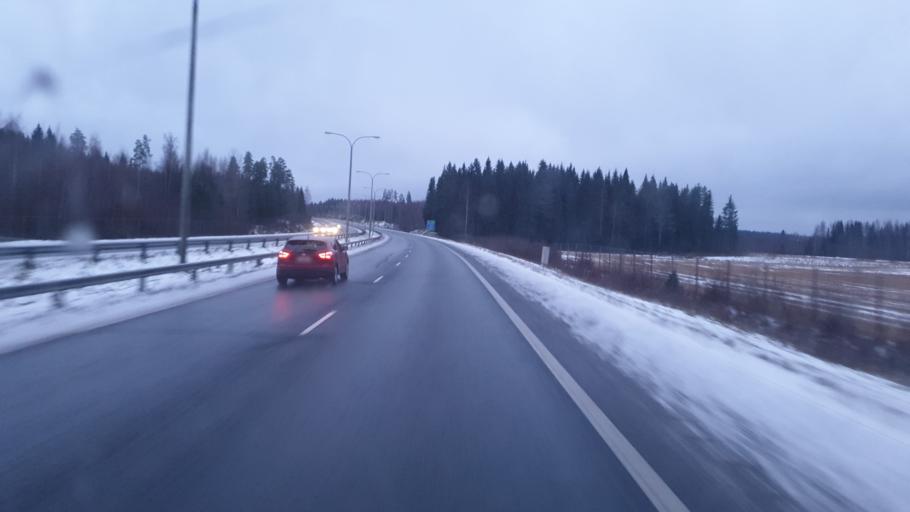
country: FI
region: Northern Savo
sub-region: Kuopio
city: Siilinjaervi
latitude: 63.0343
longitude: 27.6569
